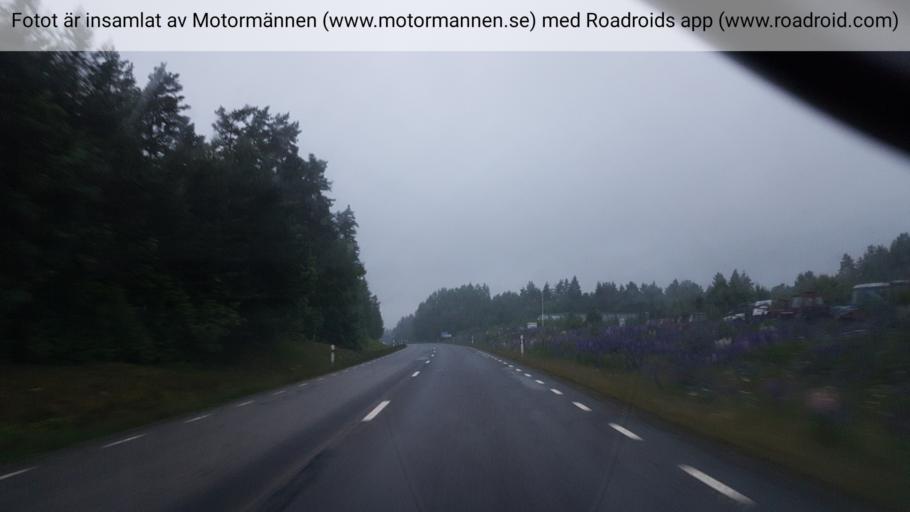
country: SE
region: Joenkoeping
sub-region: Mullsjo Kommun
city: Mullsjoe
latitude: 57.9277
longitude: 13.8516
